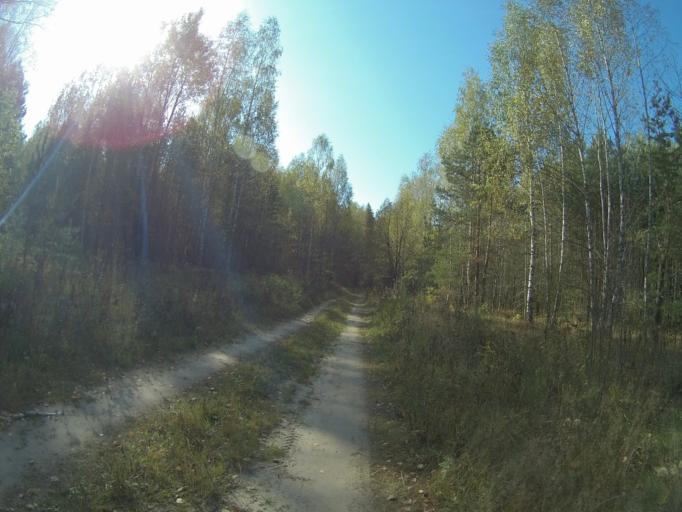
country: RU
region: Vladimir
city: Vorsha
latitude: 55.9806
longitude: 40.1457
